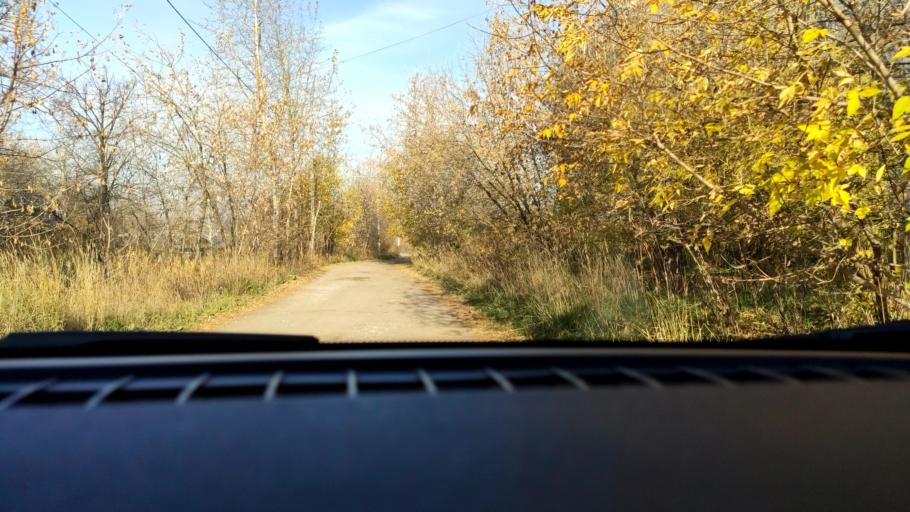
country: RU
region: Perm
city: Perm
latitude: 58.0311
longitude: 56.3193
